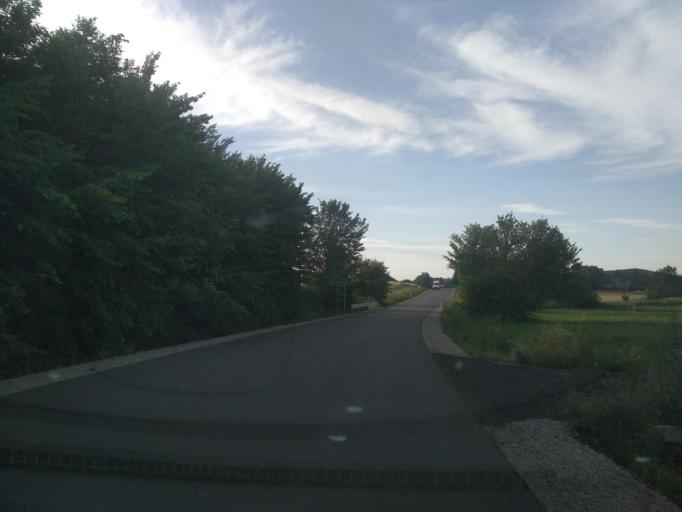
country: PL
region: Subcarpathian Voivodeship
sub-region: Powiat sanocki
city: Strachocina
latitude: 49.5955
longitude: 22.0991
